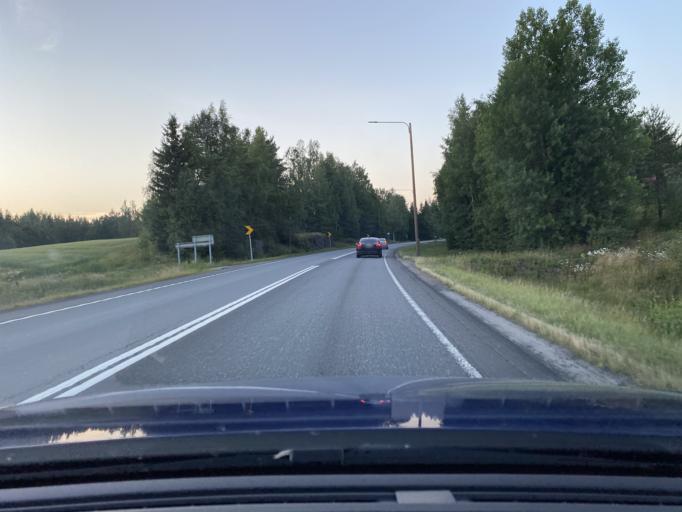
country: FI
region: Pirkanmaa
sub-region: Luoteis-Pirkanmaa
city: Ikaalinen
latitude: 61.8476
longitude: 22.9304
